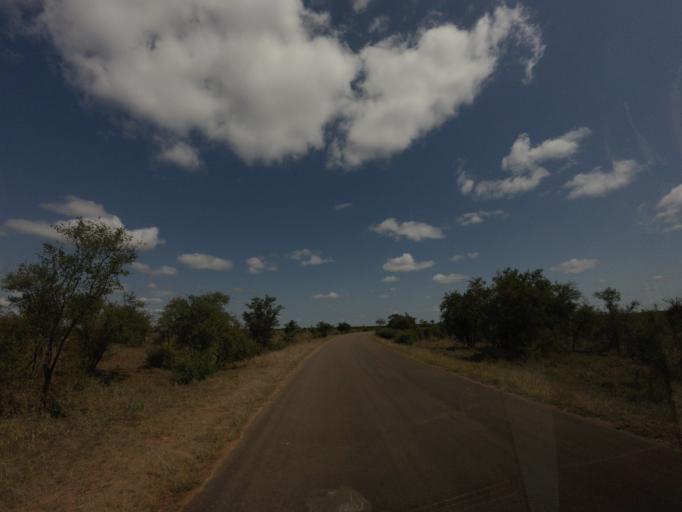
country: ZA
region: Mpumalanga
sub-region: Ehlanzeni District
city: Komatipoort
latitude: -25.0995
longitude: 31.9200
